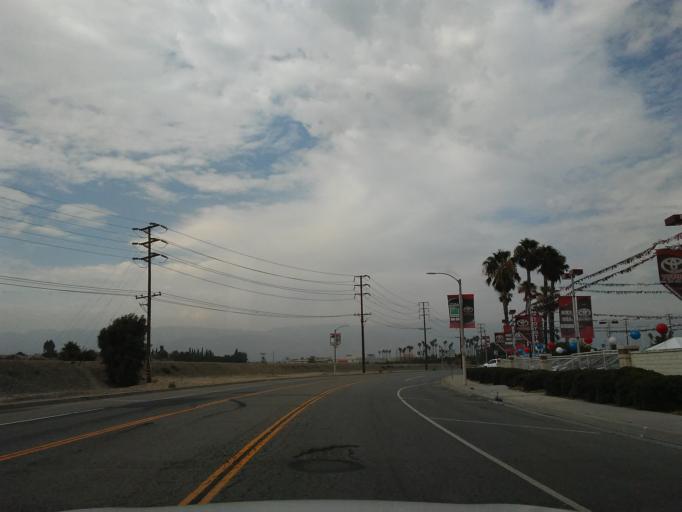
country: US
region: California
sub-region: San Bernardino County
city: Colton
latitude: 34.0734
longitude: -117.3005
